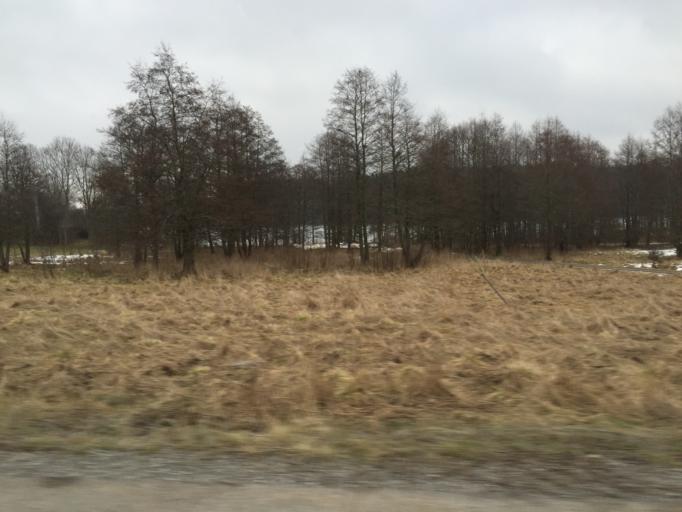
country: SE
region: Stockholm
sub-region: Salems Kommun
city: Ronninge
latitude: 59.1831
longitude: 17.7259
